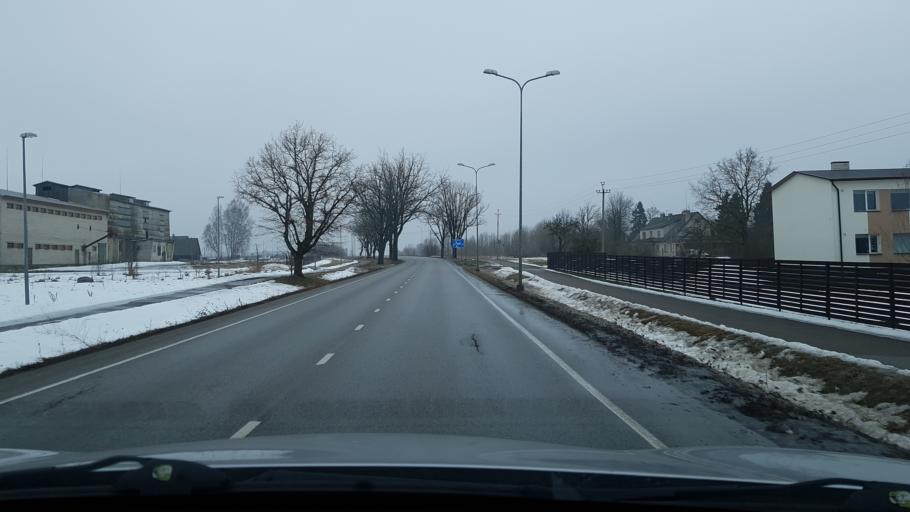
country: EE
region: Viljandimaa
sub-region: Viiratsi vald
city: Viiratsi
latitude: 58.2414
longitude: 25.8570
